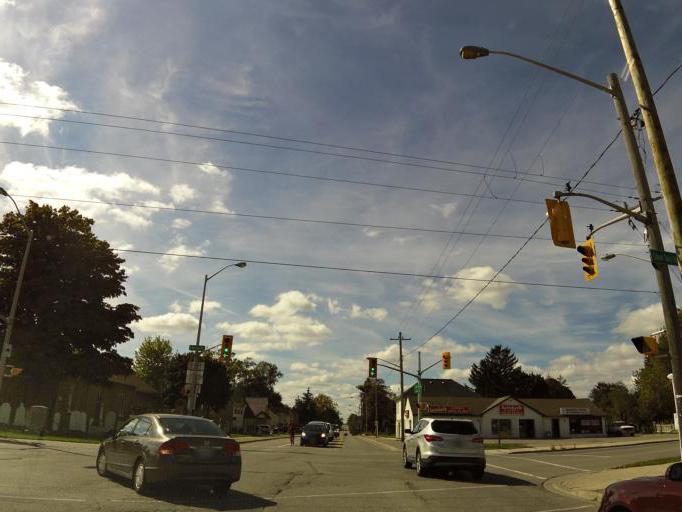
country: CA
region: Ontario
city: London
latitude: 42.9096
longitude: -81.3000
